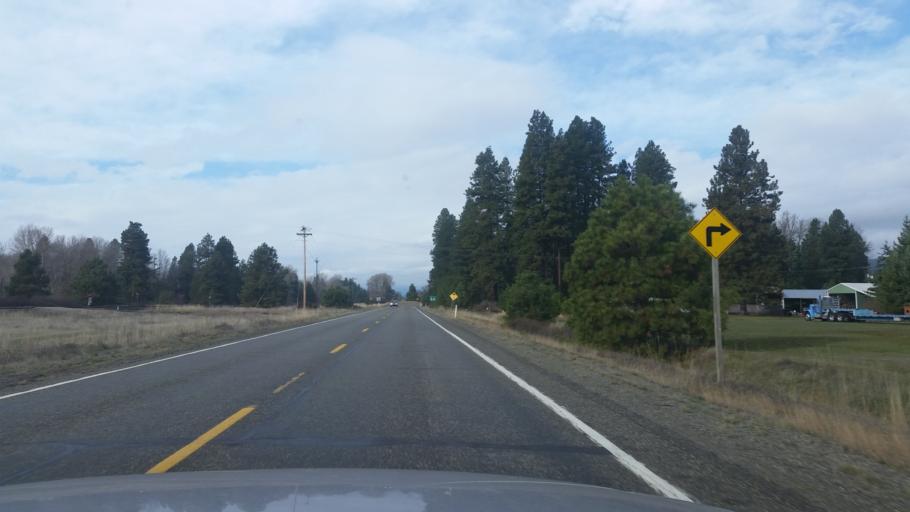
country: US
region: Washington
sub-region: Kittitas County
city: Cle Elum
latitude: 47.1730
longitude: -120.8498
